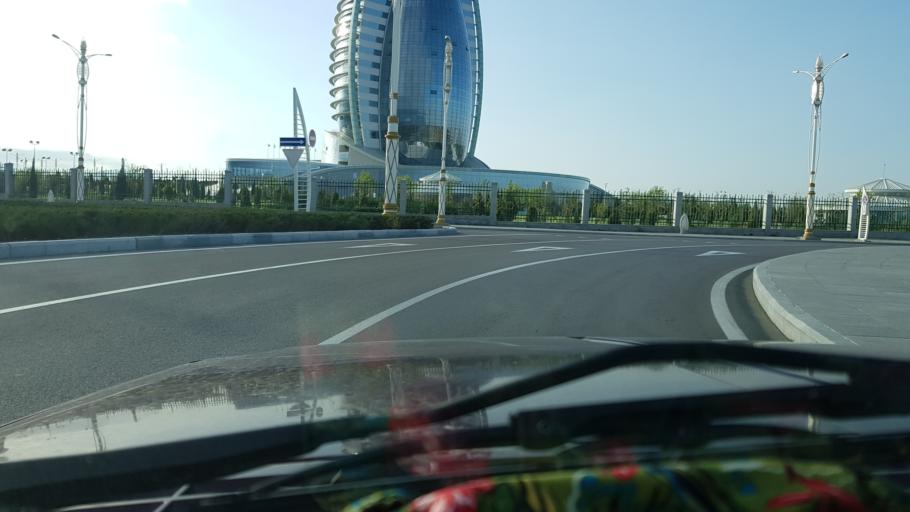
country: TM
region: Ahal
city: Ashgabat
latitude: 37.9280
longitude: 58.3355
